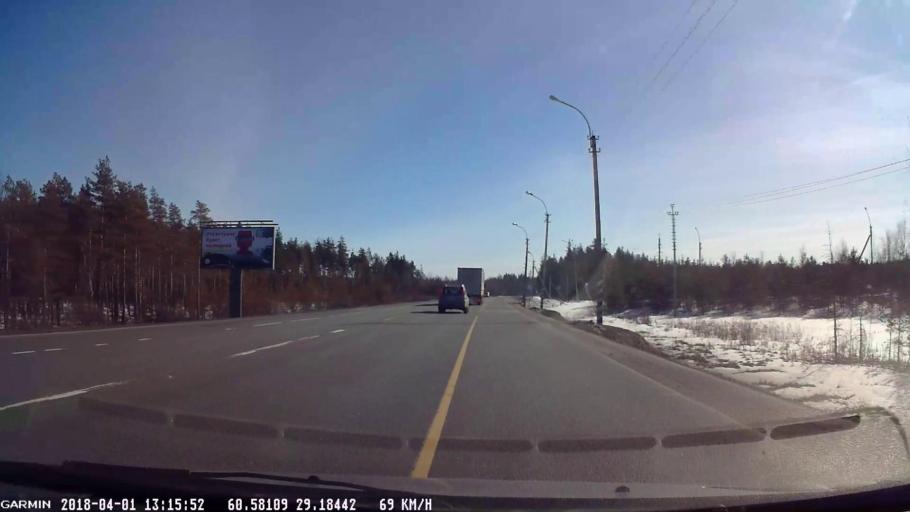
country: RU
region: Leningrad
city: Veshchevo
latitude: 60.5810
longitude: 29.1845
